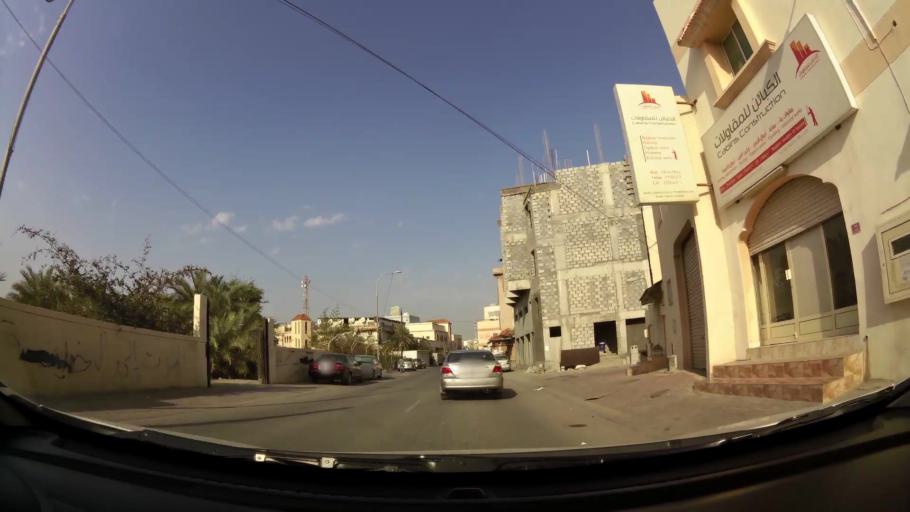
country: BH
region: Manama
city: Jidd Hafs
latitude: 26.2161
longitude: 50.5165
